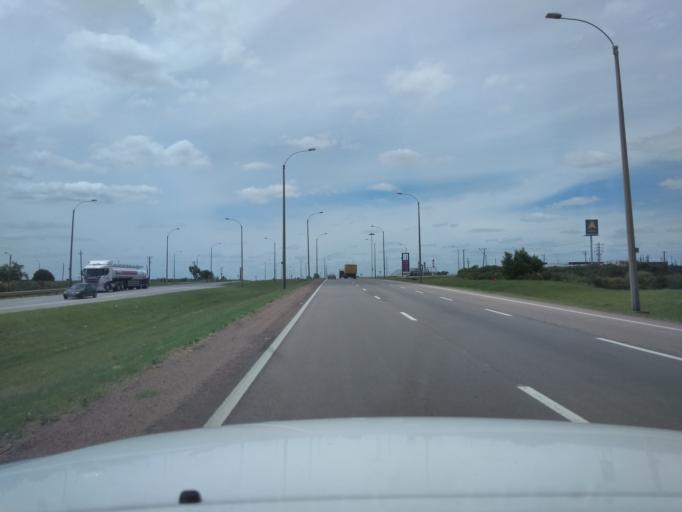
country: UY
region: Canelones
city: La Paz
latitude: -34.7522
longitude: -56.2564
